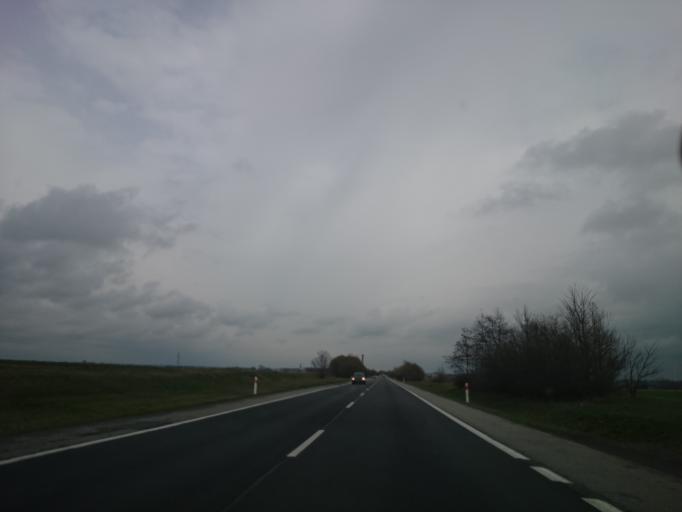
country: PL
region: Opole Voivodeship
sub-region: Powiat nyski
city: Kamienica
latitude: 50.4588
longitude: 16.9621
